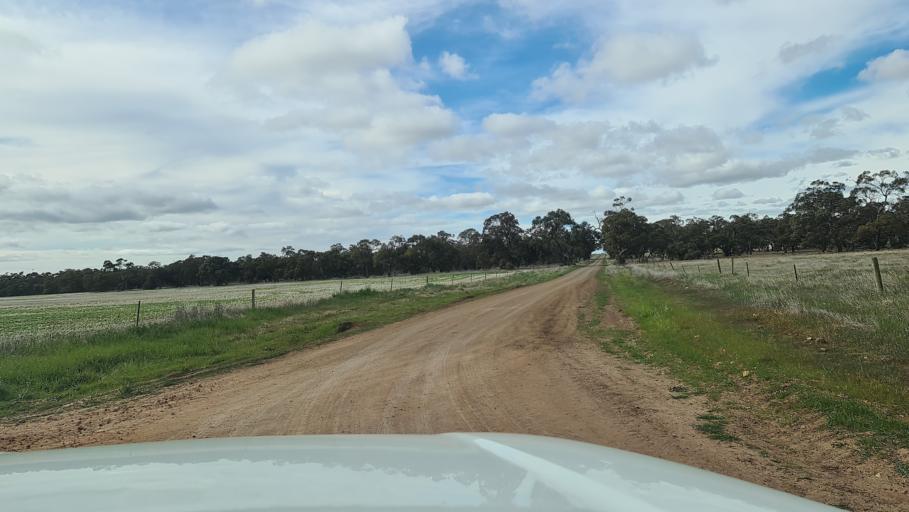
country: AU
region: Victoria
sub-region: Horsham
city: Horsham
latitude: -36.6313
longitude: 142.4118
